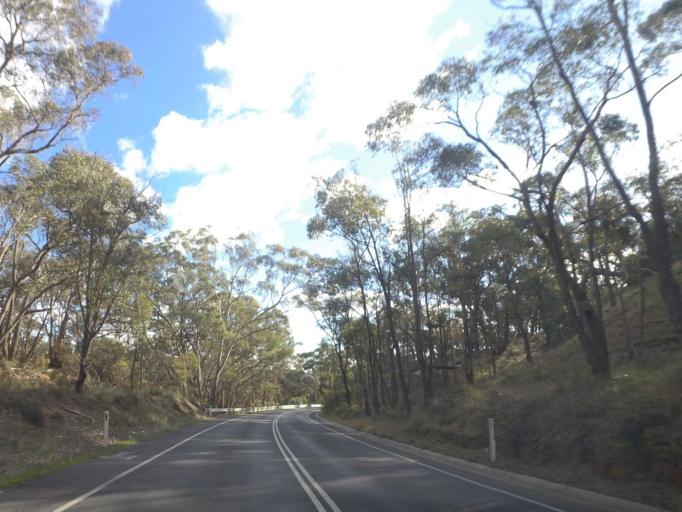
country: AU
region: Victoria
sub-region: Mount Alexander
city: Castlemaine
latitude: -37.1056
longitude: 144.3073
